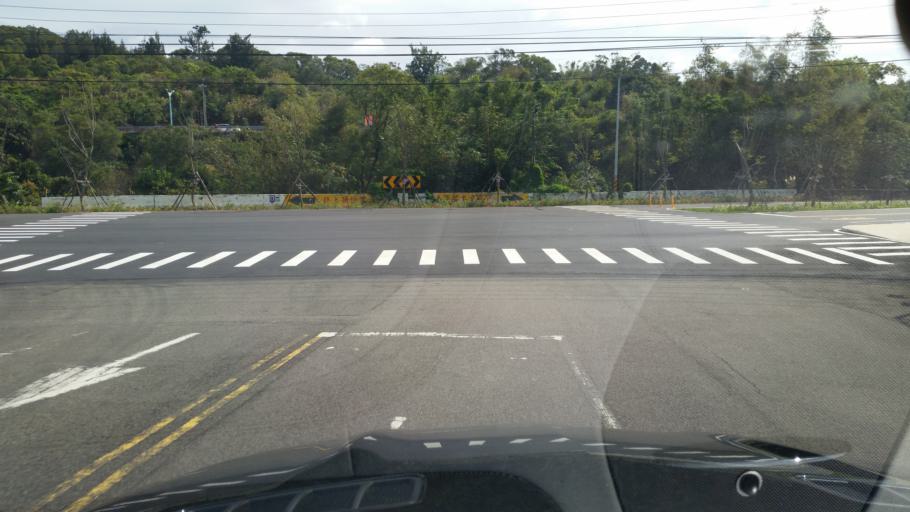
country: TW
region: Taiwan
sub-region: Miaoli
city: Miaoli
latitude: 24.6244
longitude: 120.8466
